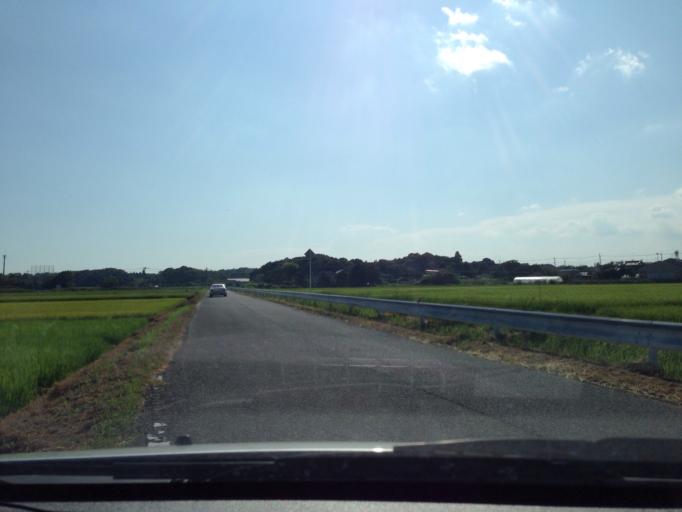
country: JP
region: Ibaraki
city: Inashiki
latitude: 35.9900
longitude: 140.3427
